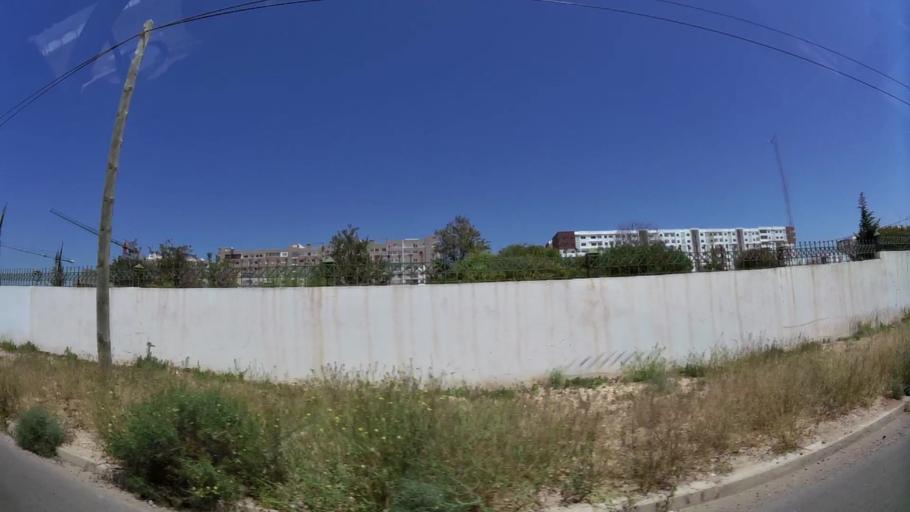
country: MA
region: Oued ed Dahab-Lagouira
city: Dakhla
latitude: 30.4340
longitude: -9.5649
